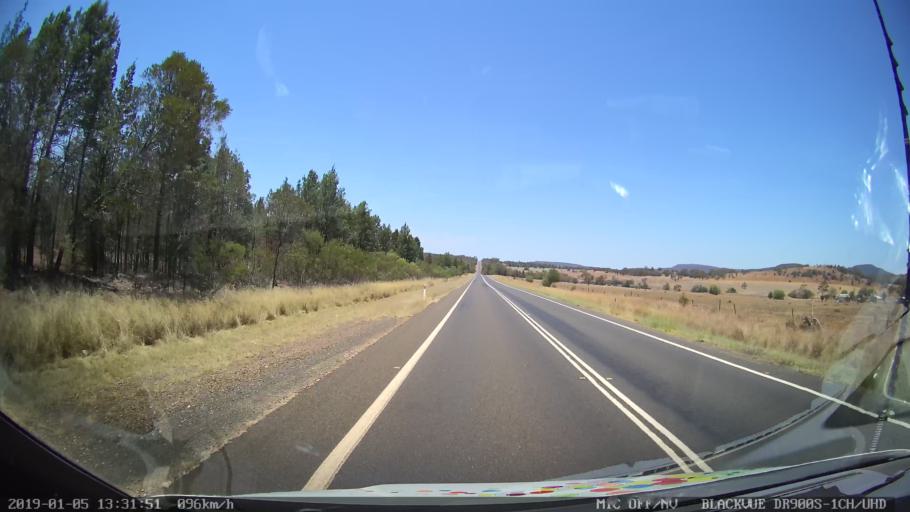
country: AU
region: New South Wales
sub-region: Gunnedah
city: Gunnedah
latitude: -31.0085
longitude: 150.0904
